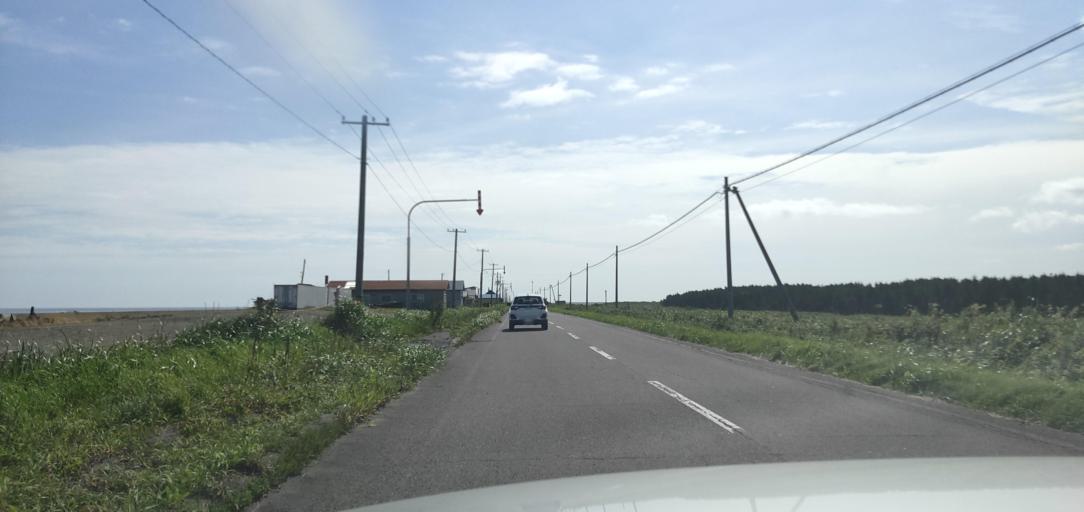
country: JP
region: Hokkaido
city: Shibetsu
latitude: 43.6363
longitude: 145.1718
